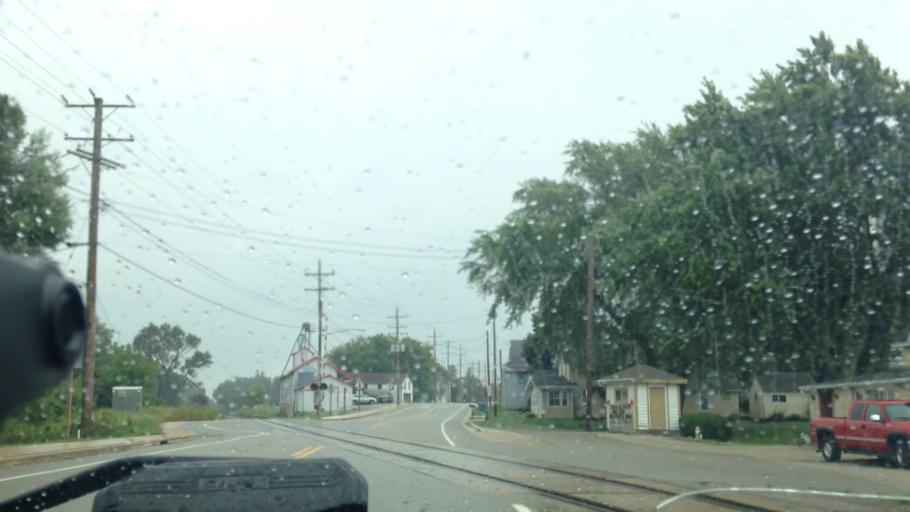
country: US
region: Wisconsin
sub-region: Washington County
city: Richfield
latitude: 43.2596
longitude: -88.1963
